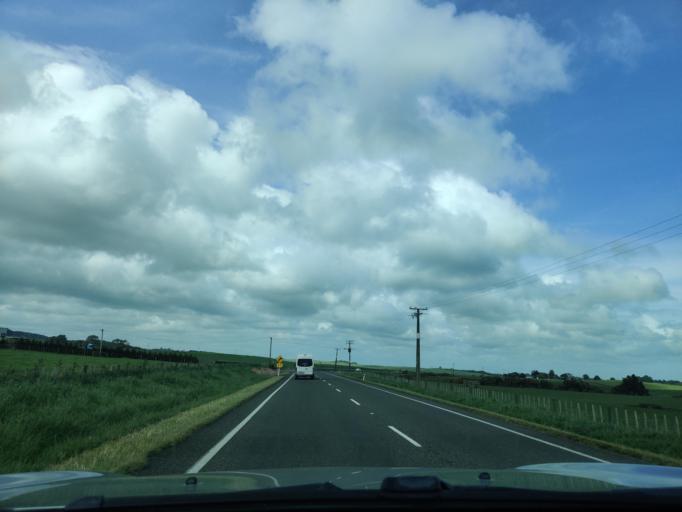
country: NZ
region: Manawatu-Wanganui
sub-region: Wanganui District
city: Wanganui
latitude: -39.8143
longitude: 174.8206
